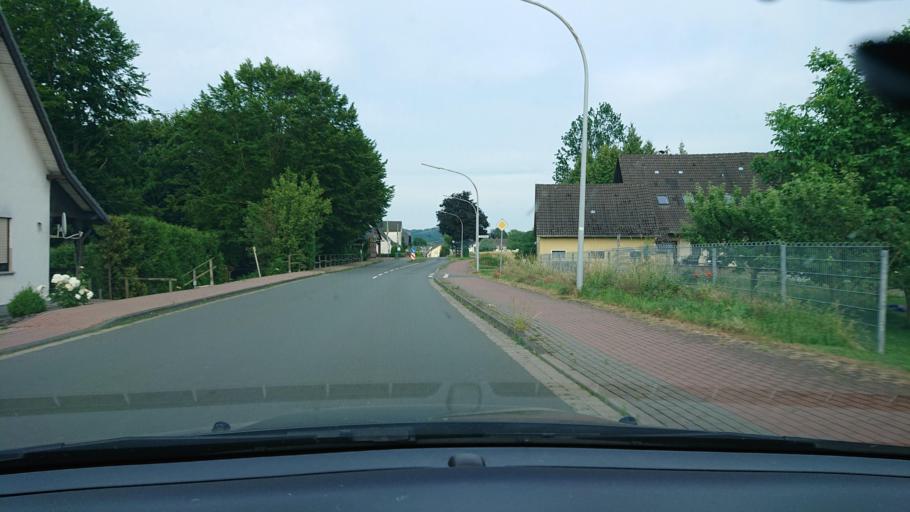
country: DE
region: North Rhine-Westphalia
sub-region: Regierungsbezirk Detmold
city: Rodinghausen
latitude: 52.2780
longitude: 8.4826
